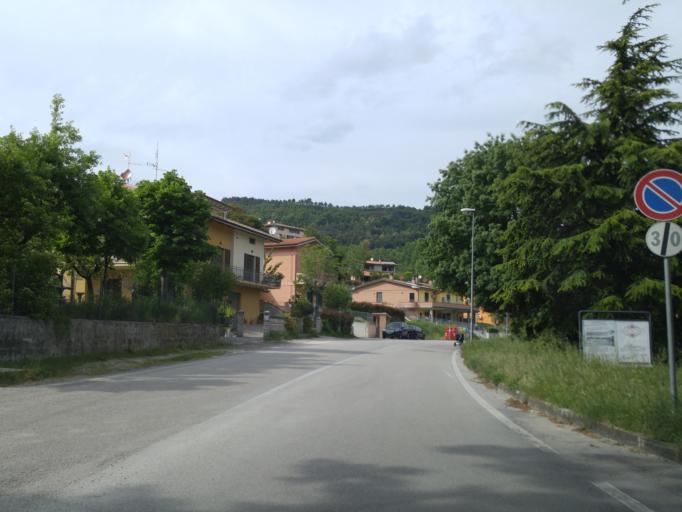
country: IT
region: The Marches
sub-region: Provincia di Pesaro e Urbino
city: Acqualagna
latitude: 43.6247
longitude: 12.6729
